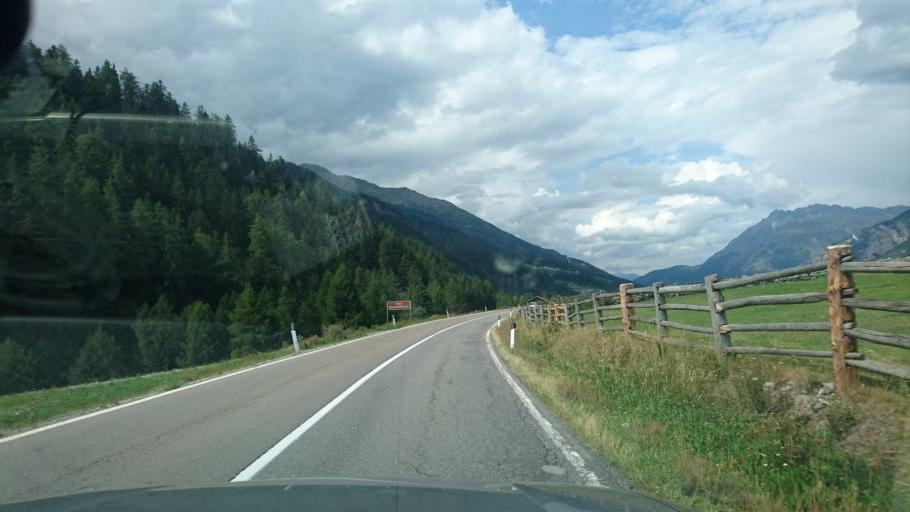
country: IT
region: Trentino-Alto Adige
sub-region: Bolzano
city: Malles Venosta
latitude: 46.7365
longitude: 10.5347
